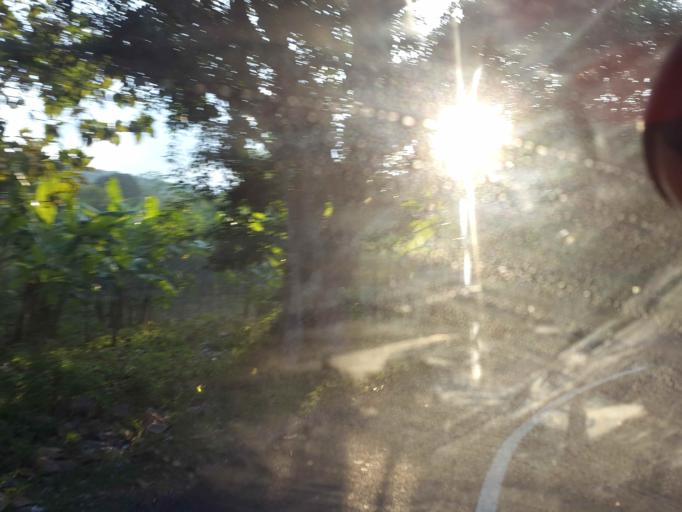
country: ID
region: Bali
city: Sampalan
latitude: -8.6889
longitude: 115.5799
